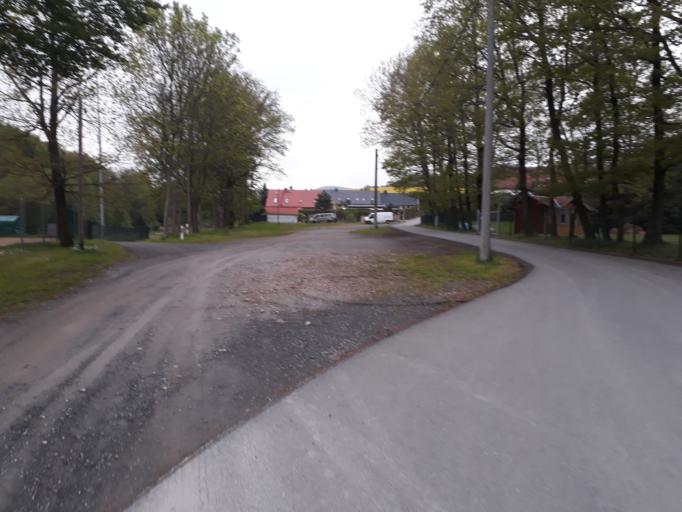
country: DE
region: Saxony
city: Reinhardtsgrimma
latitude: 50.8891
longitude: 13.7473
